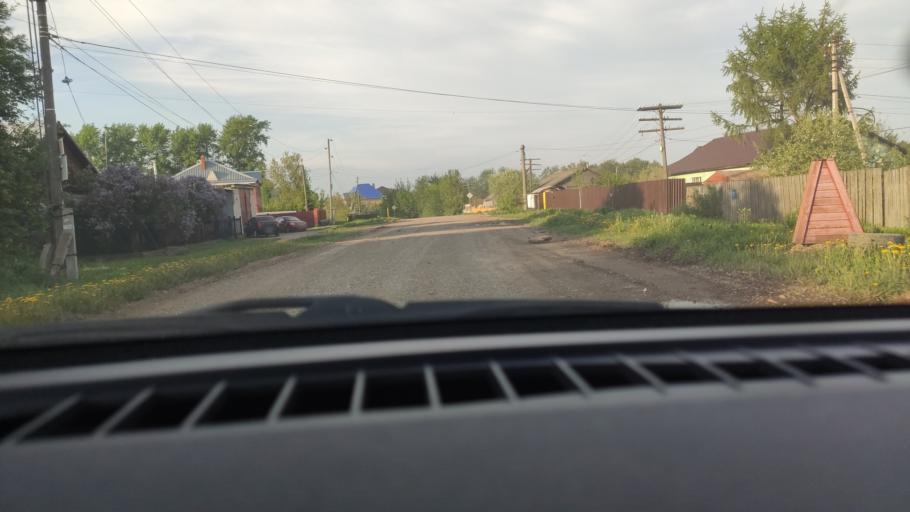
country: RU
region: Perm
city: Kultayevo
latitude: 57.9292
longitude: 56.0146
